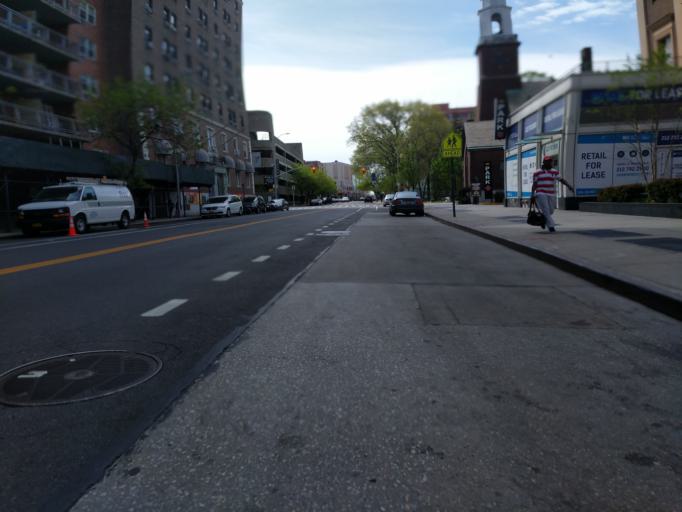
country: US
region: New York
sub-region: Queens County
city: Jamaica
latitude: 40.7055
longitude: -73.8015
